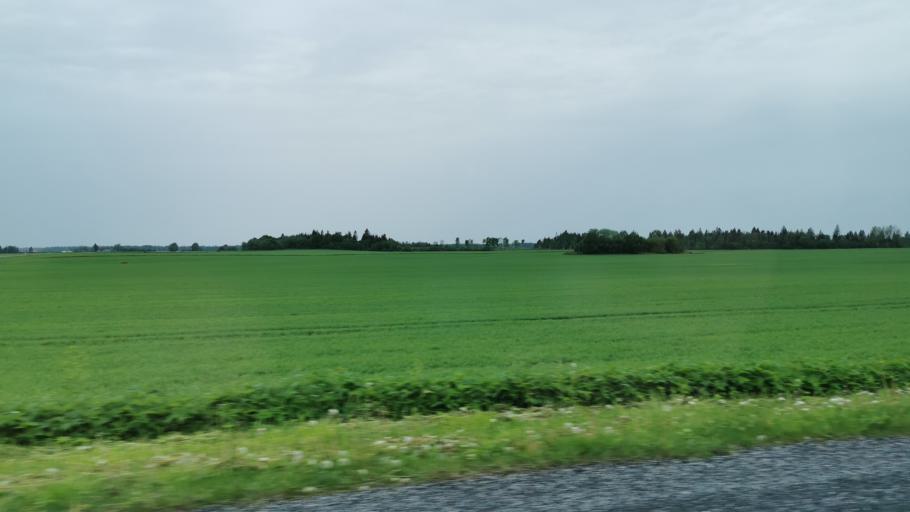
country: EE
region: Laeaene-Virumaa
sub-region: Vaeike-Maarja vald
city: Vaike-Maarja
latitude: 59.1626
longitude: 26.2943
